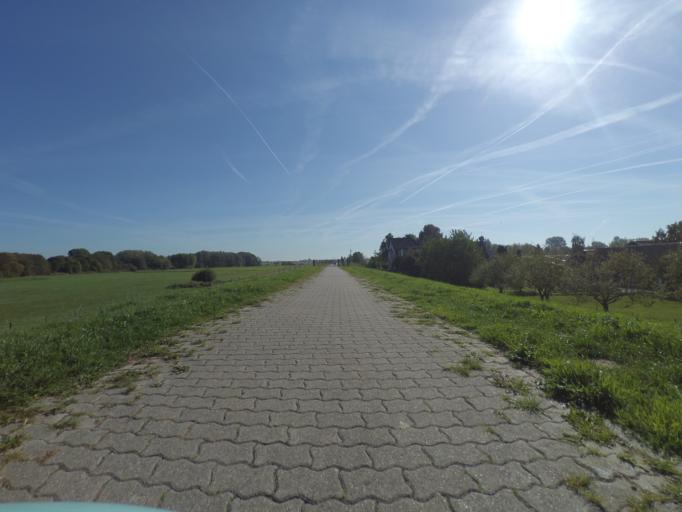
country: DE
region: North Rhine-Westphalia
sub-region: Regierungsbezirk Dusseldorf
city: Kleve
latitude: 51.8447
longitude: 6.0889
